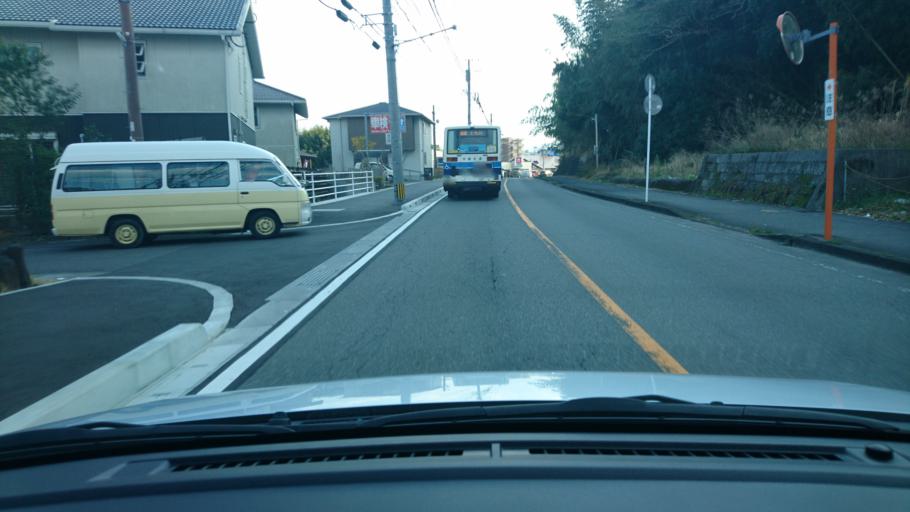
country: JP
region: Miyazaki
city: Miyazaki-shi
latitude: 31.8781
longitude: 131.4058
